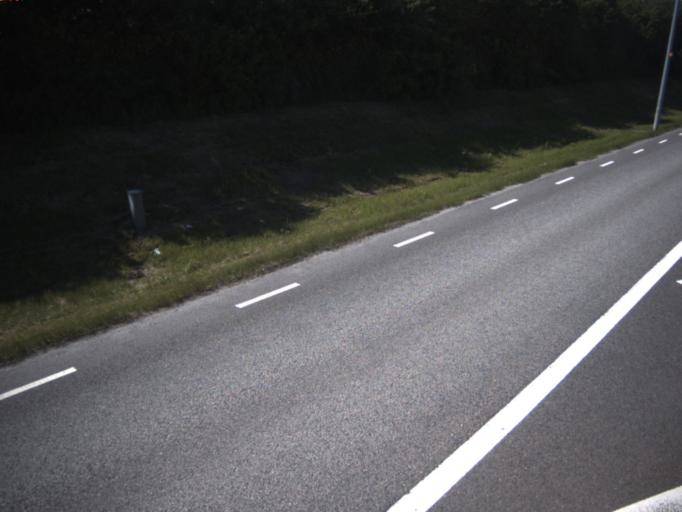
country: SE
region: Skane
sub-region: Helsingborg
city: Barslov
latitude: 56.0367
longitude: 12.7803
